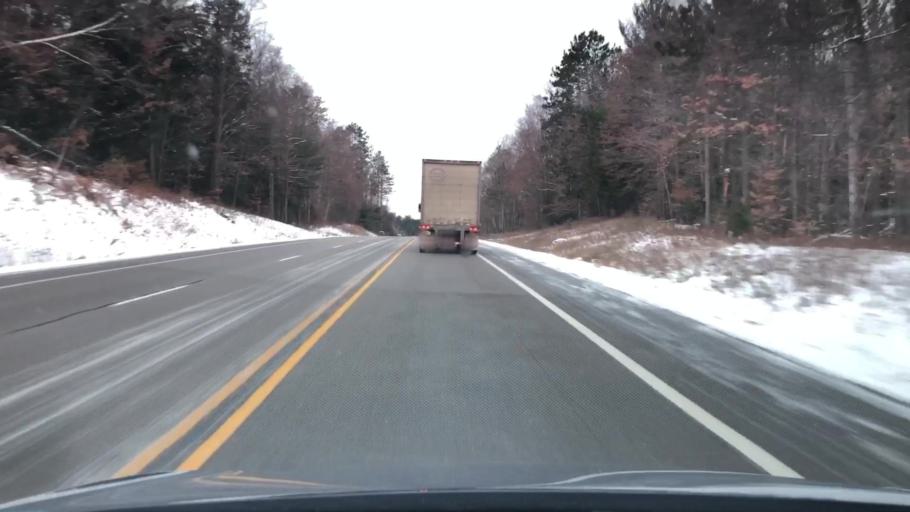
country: US
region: Michigan
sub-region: Wexford County
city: Cadillac
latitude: 44.1873
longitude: -85.3890
